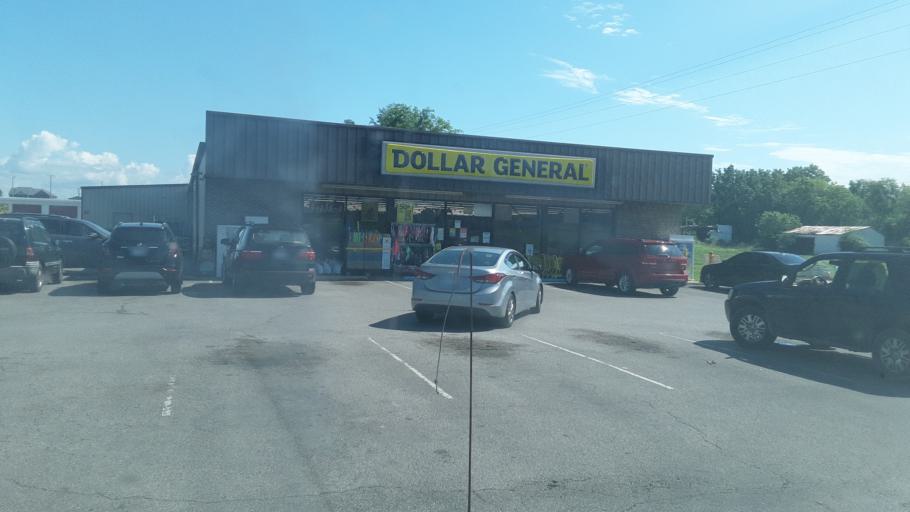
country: US
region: Kentucky
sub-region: Todd County
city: Elkton
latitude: 36.8136
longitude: -87.1715
